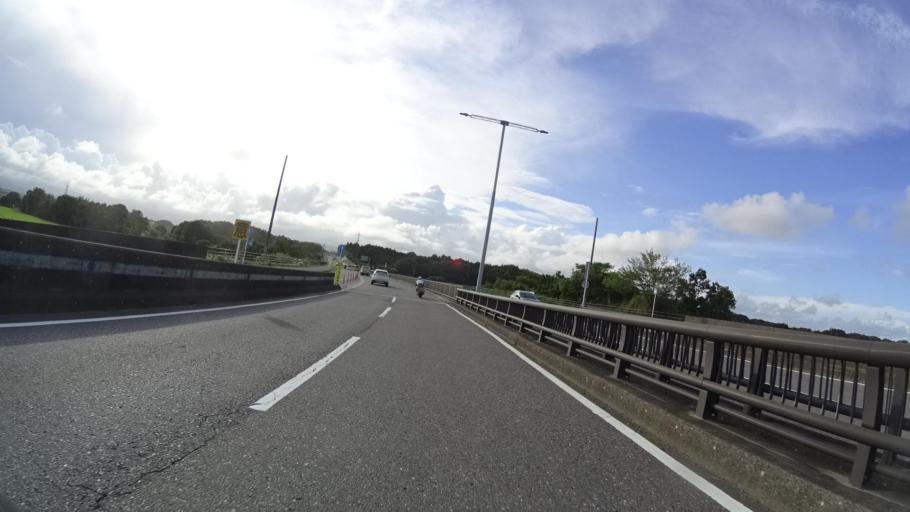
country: JP
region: Mie
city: Suzuka
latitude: 34.8795
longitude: 136.5202
